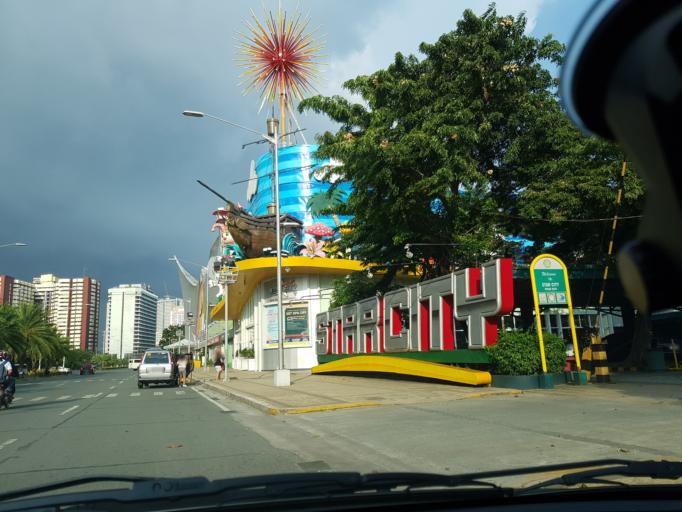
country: PH
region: Metro Manila
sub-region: City of Manila
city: Port Area
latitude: 14.5566
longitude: 120.9845
